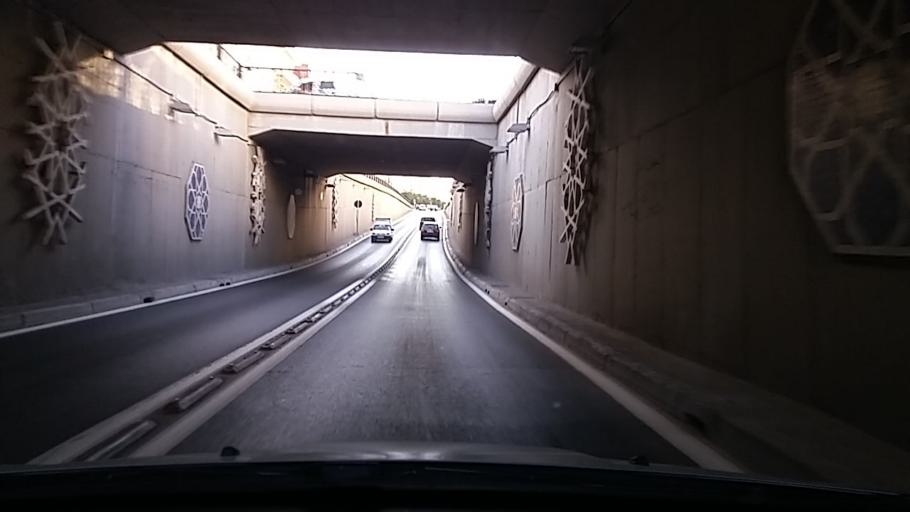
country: MA
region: Tanger-Tetouan
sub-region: Tanger-Assilah
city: Tangier
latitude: 35.7717
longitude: -5.8141
